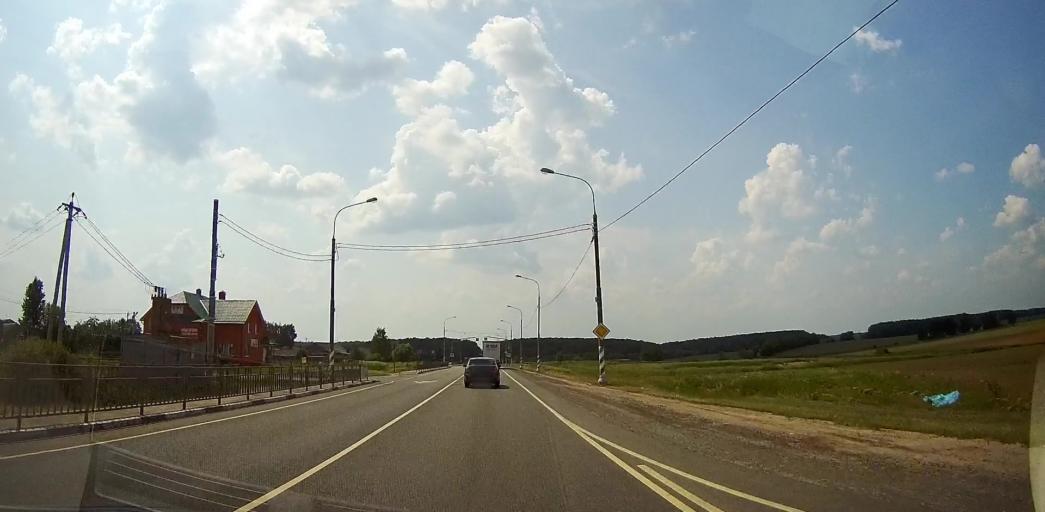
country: RU
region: Moskovskaya
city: Malino
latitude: 55.1267
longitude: 38.2398
